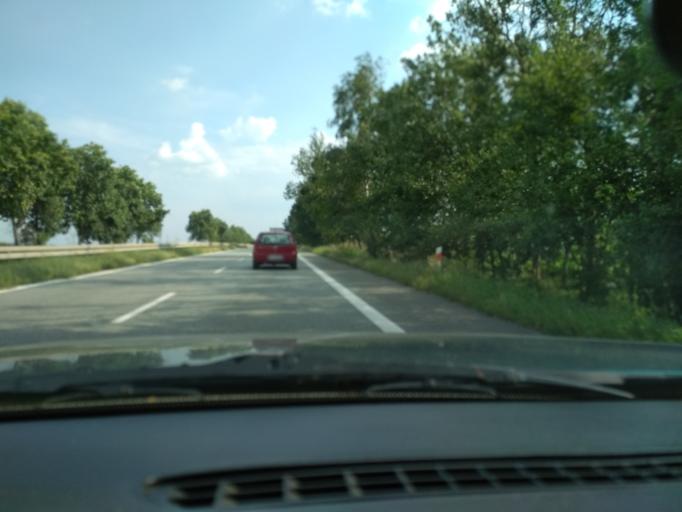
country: PL
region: Silesian Voivodeship
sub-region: Powiat pszczynski
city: Krzyzowice
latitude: 50.0043
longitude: 18.7102
